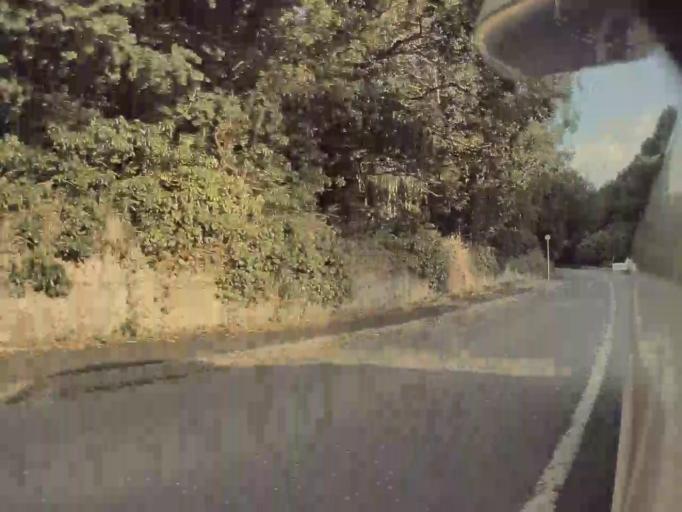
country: IE
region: Leinster
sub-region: Wicklow
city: Enniskerry
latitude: 53.2205
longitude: -6.1817
